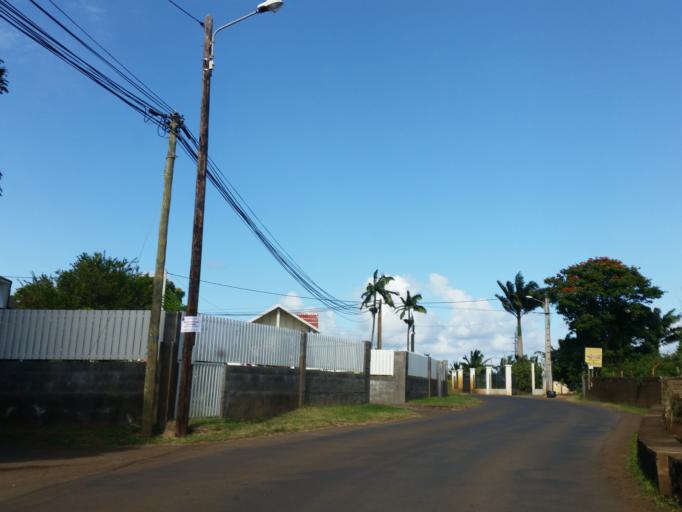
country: RE
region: Reunion
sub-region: Reunion
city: Saint-Pierre
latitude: -21.3285
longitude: 55.4950
